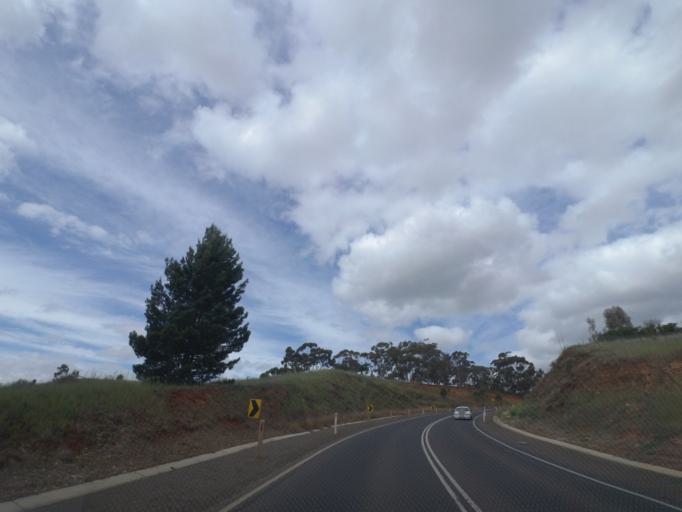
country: AU
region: Victoria
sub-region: Melton
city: Melton South
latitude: -37.7473
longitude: 144.5781
